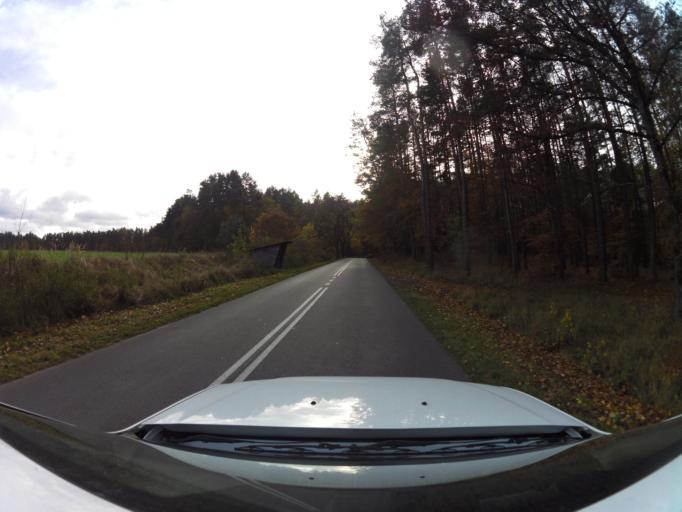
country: PL
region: West Pomeranian Voivodeship
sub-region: Powiat gryficki
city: Gryfice
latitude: 53.8558
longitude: 15.1167
